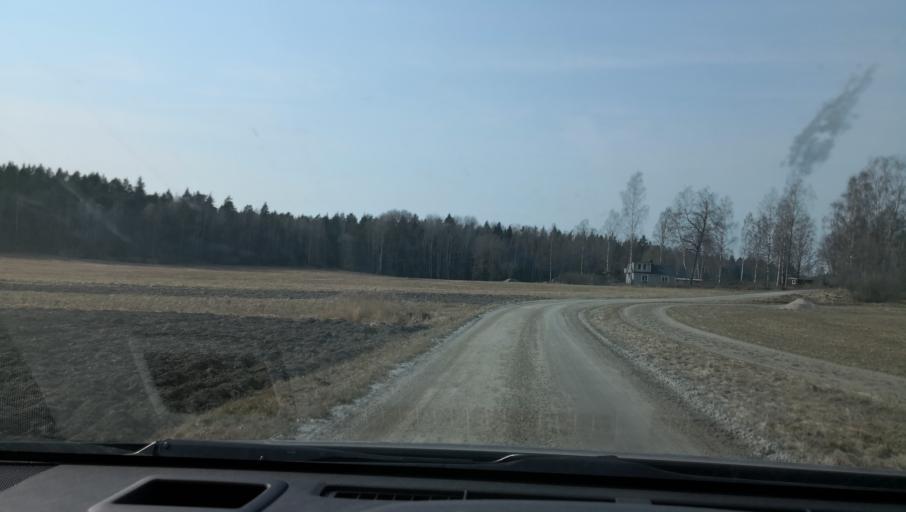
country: SE
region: OErebro
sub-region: Lindesbergs Kommun
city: Frovi
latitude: 59.3472
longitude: 15.4415
